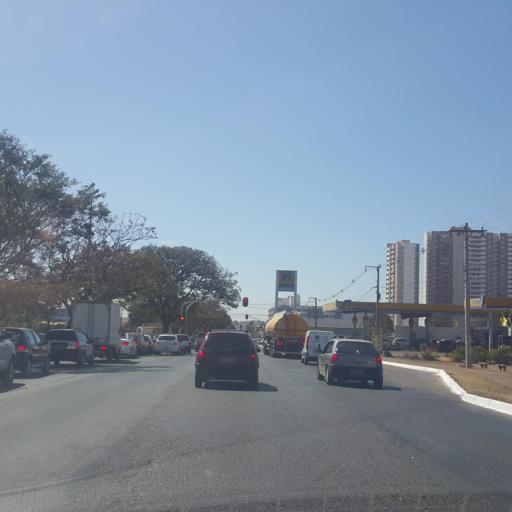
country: BR
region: Federal District
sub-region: Brasilia
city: Brasilia
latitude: -15.8086
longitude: -48.0848
